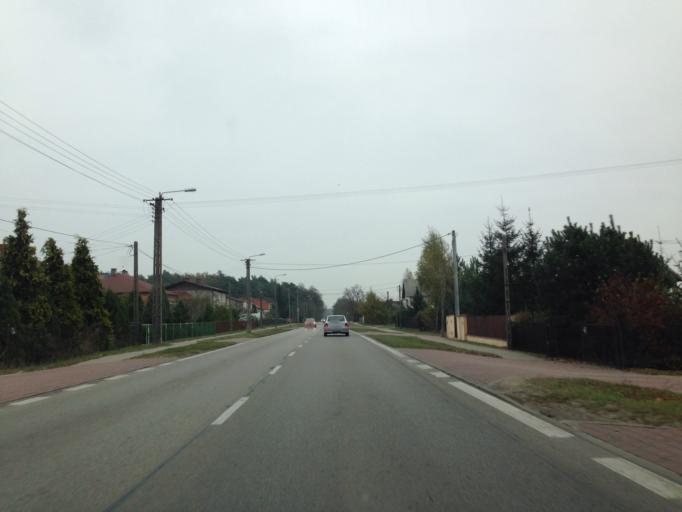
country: PL
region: Masovian Voivodeship
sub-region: Powiat warszawski zachodni
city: Leszno
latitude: 52.2621
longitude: 20.6319
